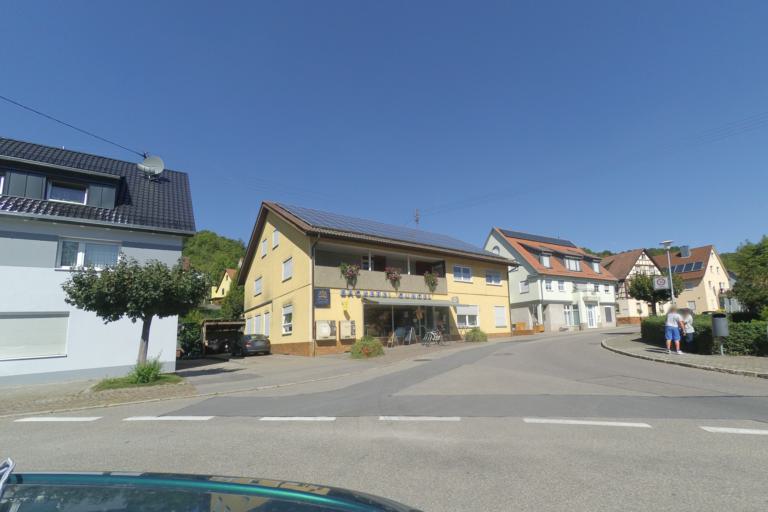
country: DE
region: Baden-Wuerttemberg
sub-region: Regierungsbezirk Stuttgart
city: Zweiflingen
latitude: 49.2912
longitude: 9.5128
